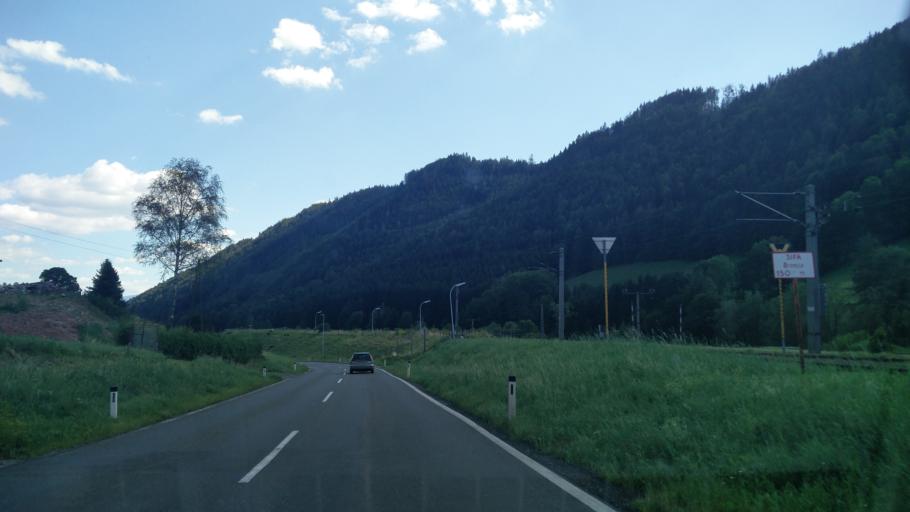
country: AT
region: Styria
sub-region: Politischer Bezirk Leoben
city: Vordernberg
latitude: 47.4694
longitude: 14.9881
